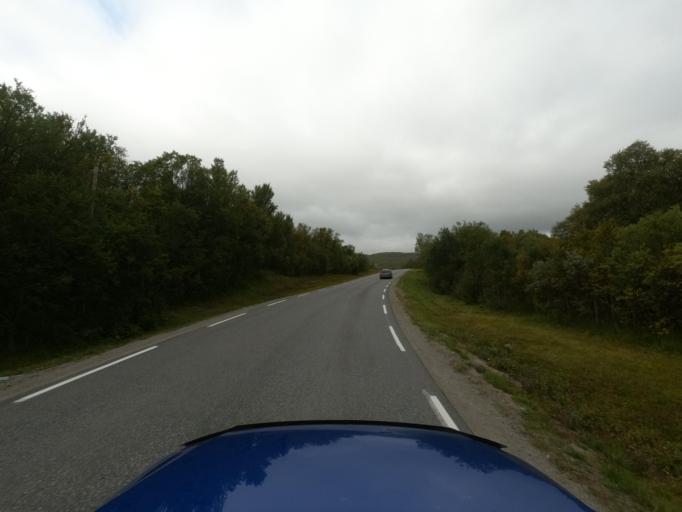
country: NO
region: Finnmark Fylke
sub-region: Porsanger
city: Lakselv
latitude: 70.3476
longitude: 25.0455
